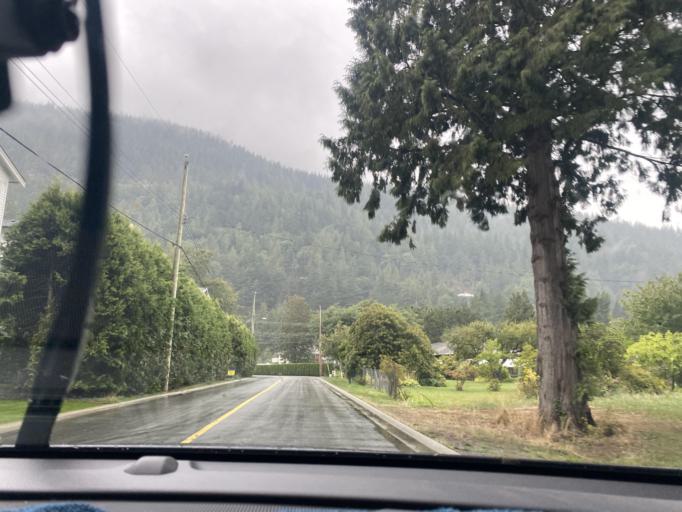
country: CA
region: British Columbia
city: Agassiz
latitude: 49.2942
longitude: -121.7804
